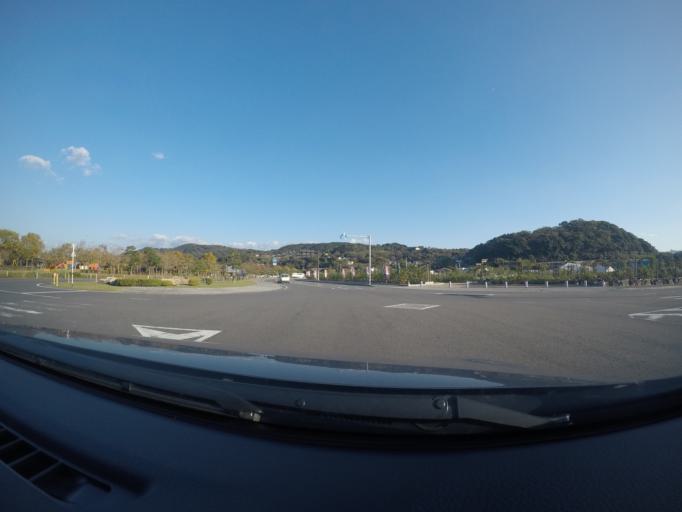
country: JP
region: Kumamoto
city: Minamata
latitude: 32.2002
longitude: 130.3823
